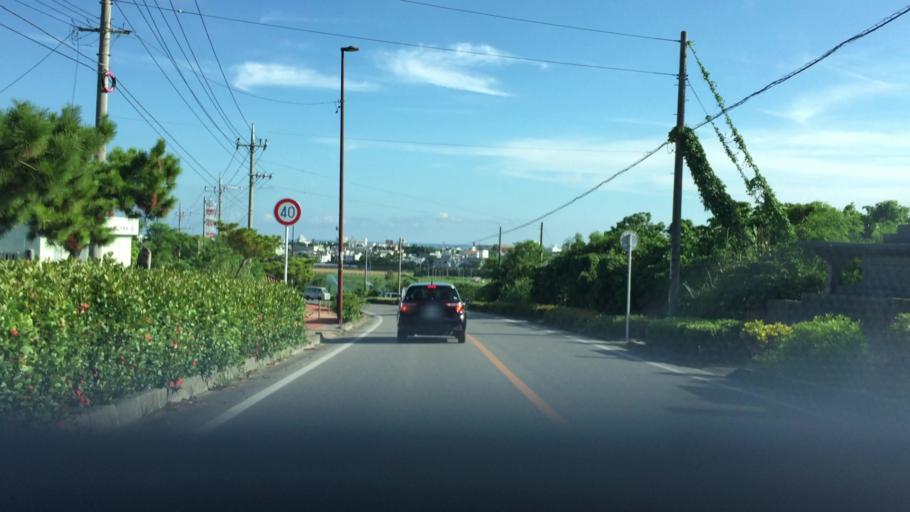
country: JP
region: Okinawa
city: Ishigaki
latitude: 24.3592
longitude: 124.1569
